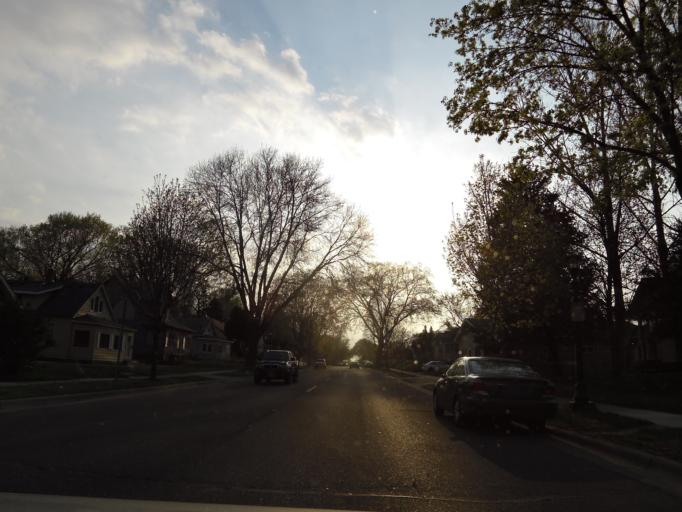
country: US
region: Minnesota
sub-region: Ramsey County
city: Maplewood
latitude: 44.9631
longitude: -93.0209
